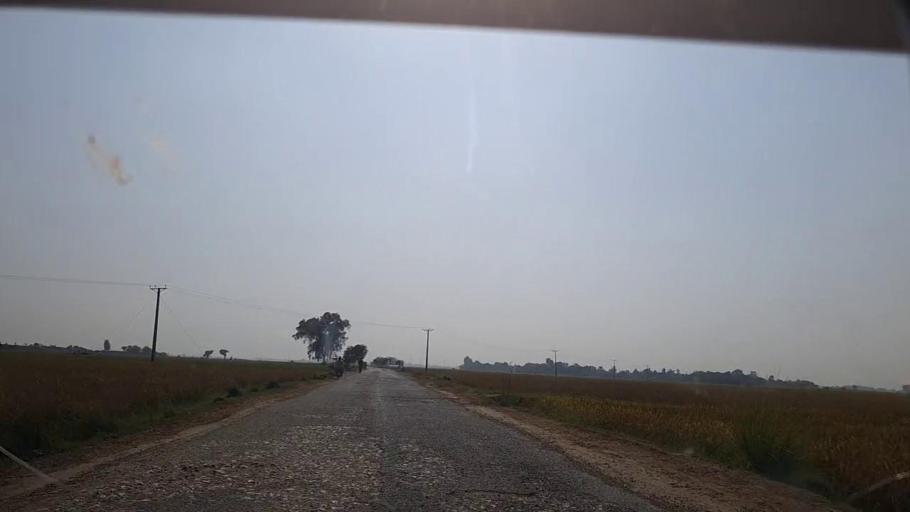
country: PK
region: Sindh
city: Shikarpur
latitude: 28.0947
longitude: 68.6095
